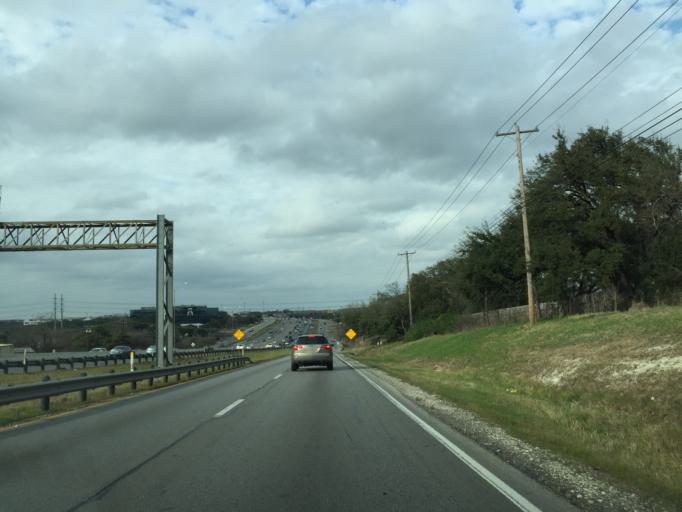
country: US
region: Texas
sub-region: Travis County
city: Wells Branch
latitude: 30.3851
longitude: -97.6729
